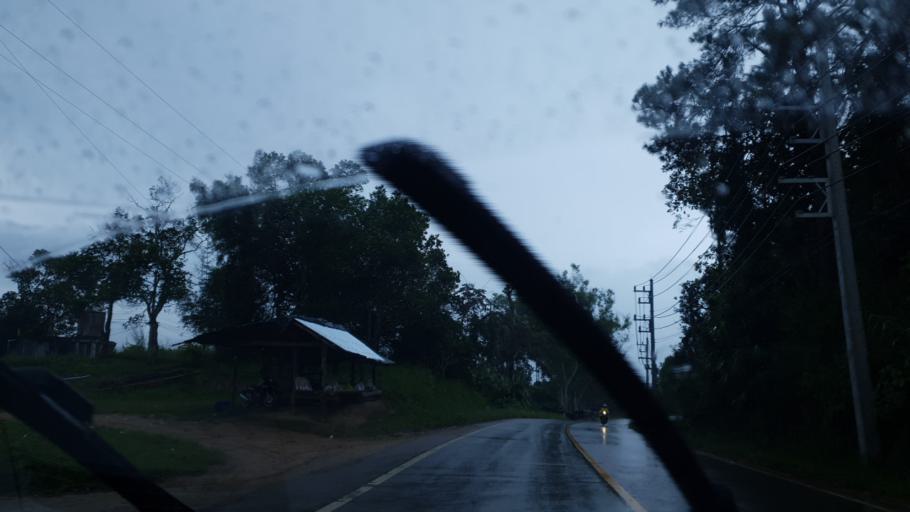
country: TH
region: Mae Hong Son
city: Pa Pae
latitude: 18.1557
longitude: 98.2869
